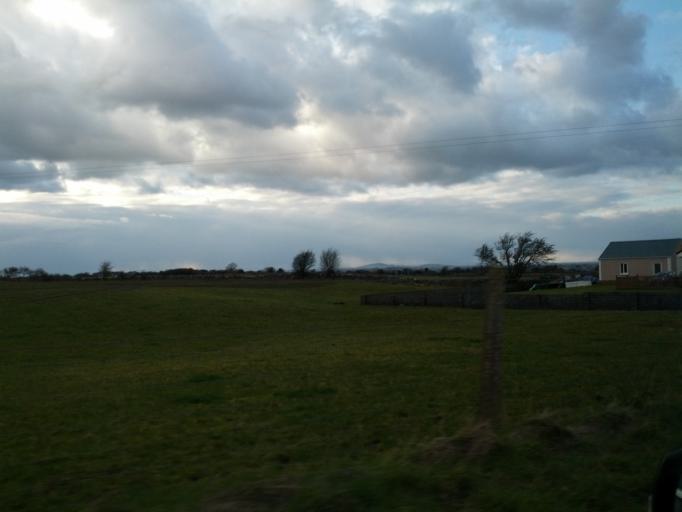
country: IE
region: Connaught
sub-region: County Galway
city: Athenry
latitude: 53.4178
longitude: -8.7522
